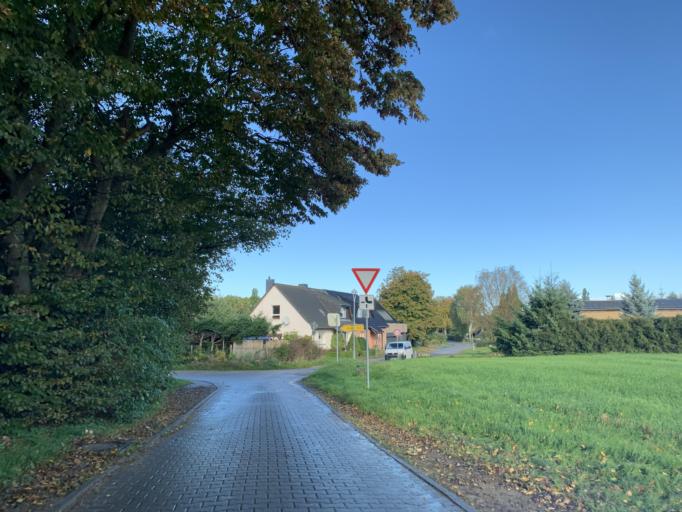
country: DE
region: Mecklenburg-Vorpommern
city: Burg Stargard
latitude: 53.4634
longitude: 13.2736
